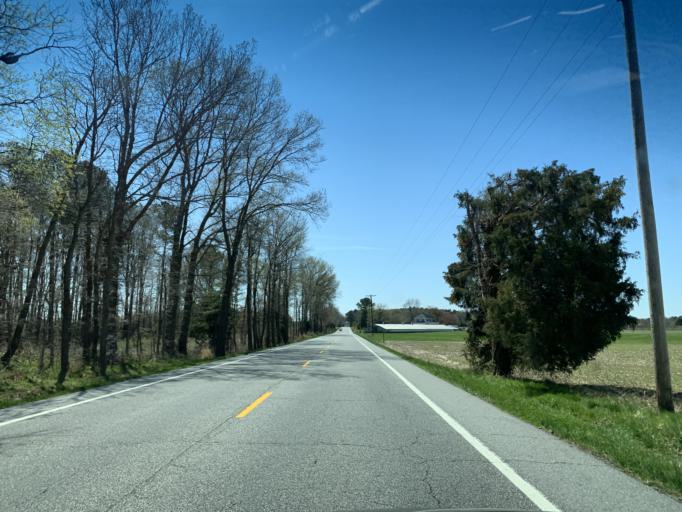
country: US
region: Maryland
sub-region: Talbot County
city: Easton
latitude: 38.8570
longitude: -76.0114
